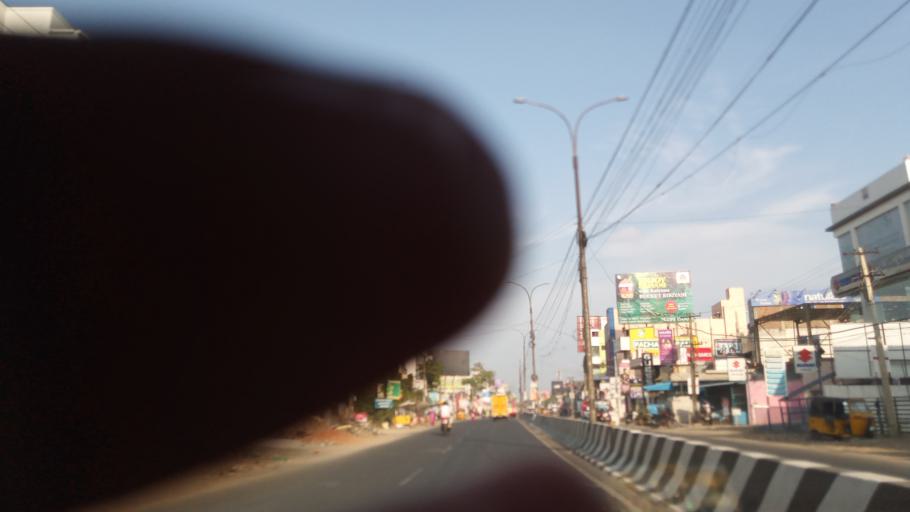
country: IN
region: Tamil Nadu
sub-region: Kancheepuram
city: Poonamalle
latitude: 13.0434
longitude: 80.1221
